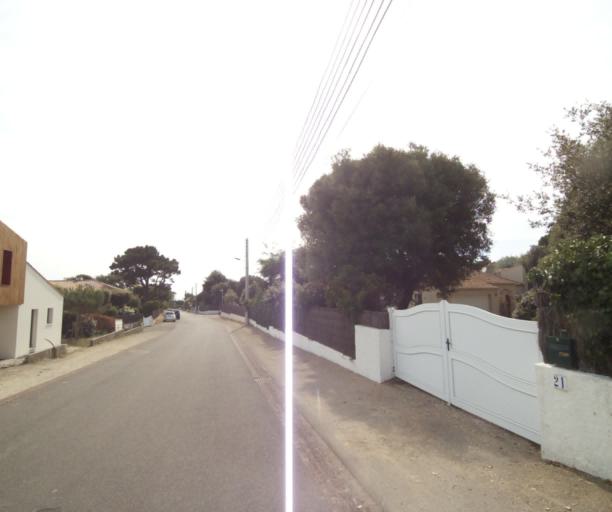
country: FR
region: Pays de la Loire
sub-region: Departement de la Vendee
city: Chateau-d'Olonne
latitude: 46.4794
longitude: -1.7543
